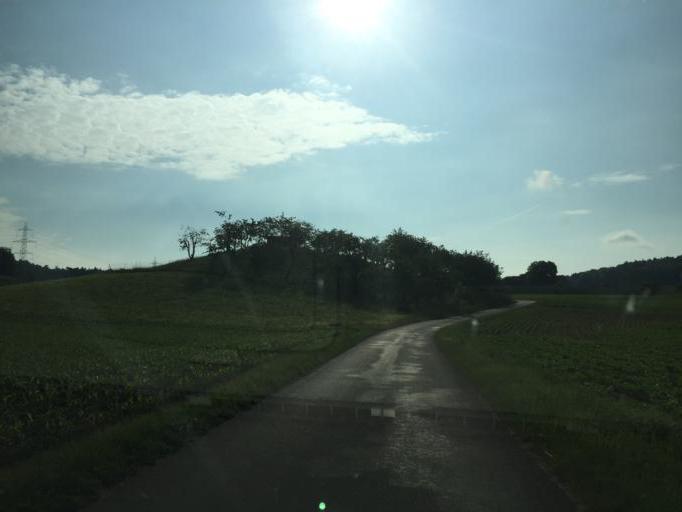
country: CH
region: Zurich
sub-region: Bezirk Buelach
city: Buelach / Gstueckt
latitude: 47.5306
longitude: 8.5494
